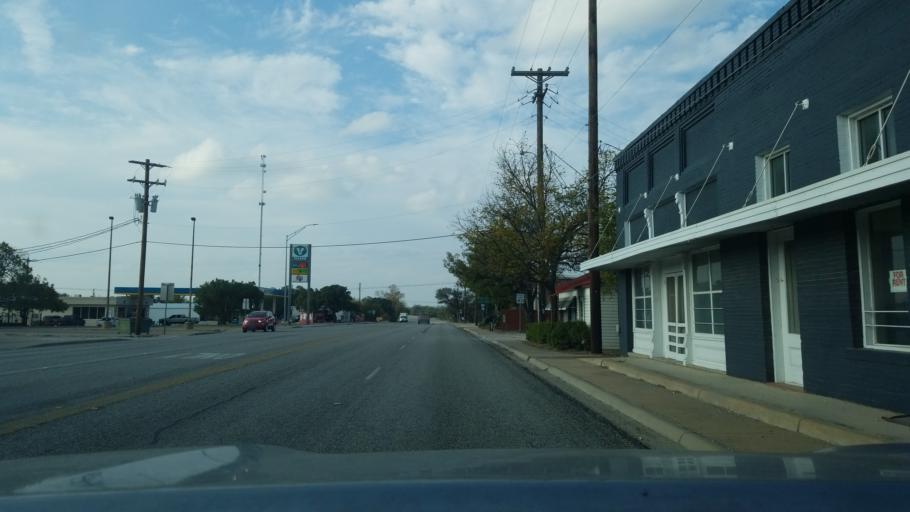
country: US
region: Texas
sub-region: Lampasas County
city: Lampasas
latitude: 31.2166
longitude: -98.3939
